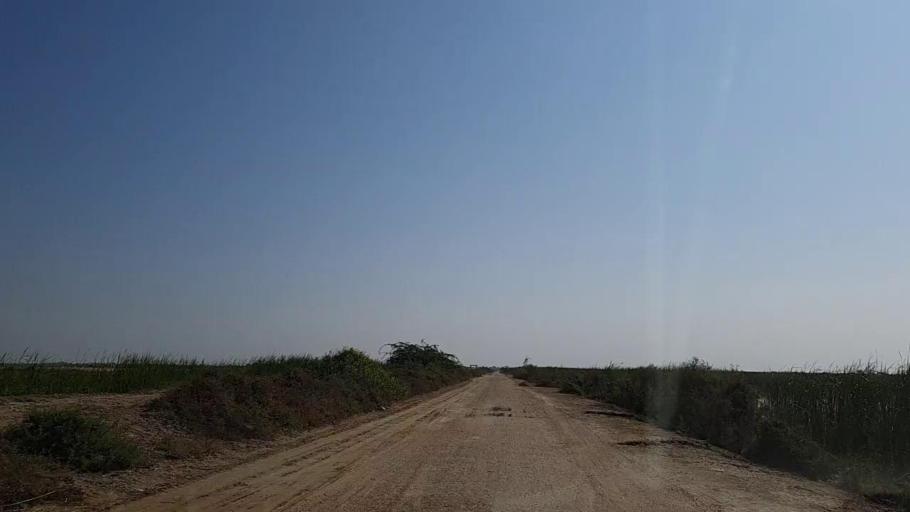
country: PK
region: Sindh
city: Chuhar Jamali
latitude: 24.4684
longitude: 68.0943
